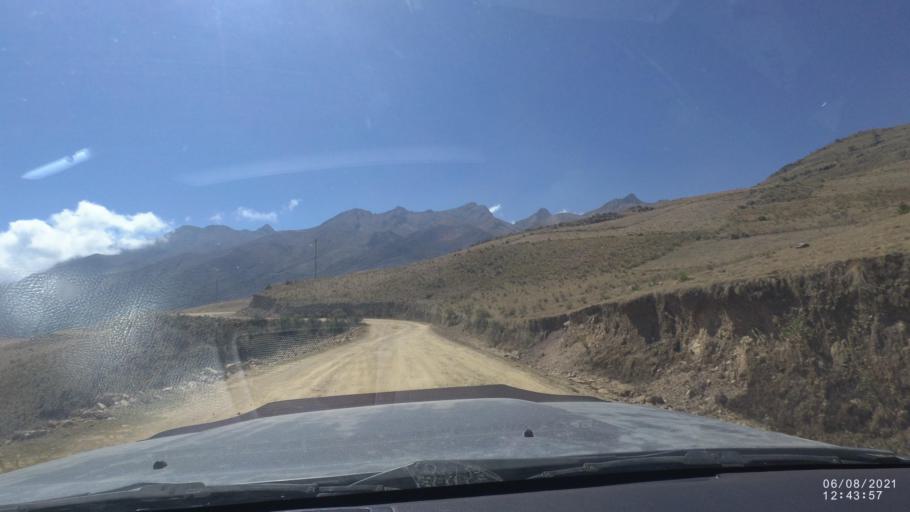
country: BO
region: Cochabamba
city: Colchani
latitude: -16.7708
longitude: -66.6668
